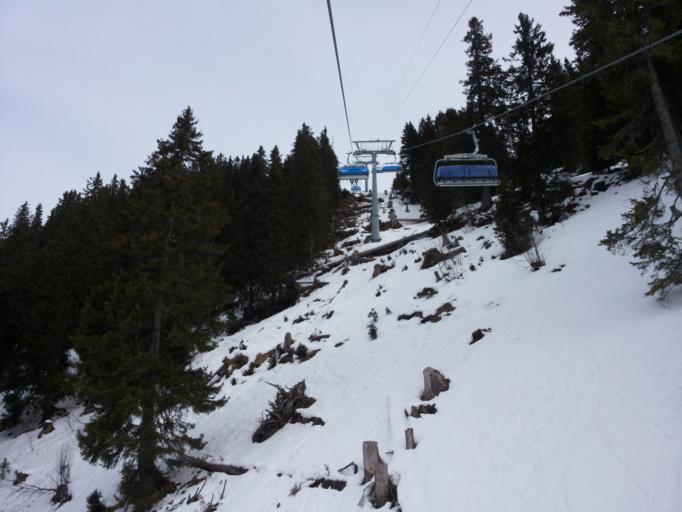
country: CH
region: Bern
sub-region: Interlaken-Oberhasli District
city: Meiringen
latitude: 46.7512
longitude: 8.2233
